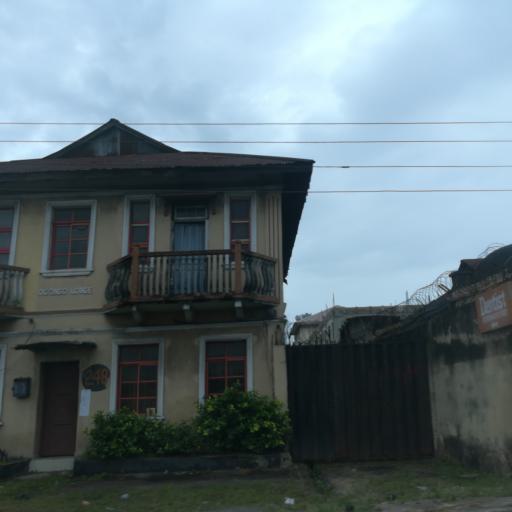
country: NG
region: Lagos
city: Makoko
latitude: 6.4960
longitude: 3.3773
